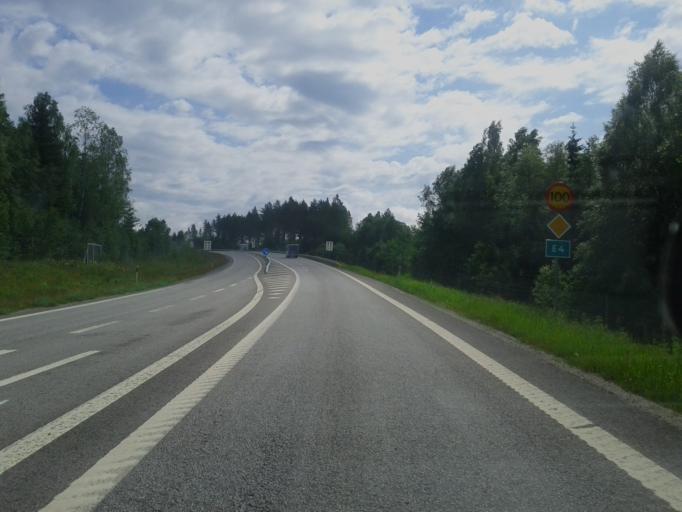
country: SE
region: Vaesternorrland
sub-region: OErnskoeldsviks Kommun
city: Ornskoldsvik
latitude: 63.2978
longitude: 18.8692
